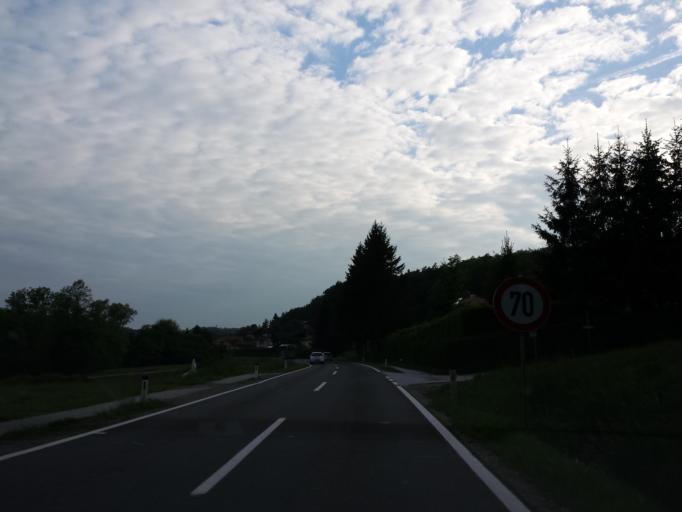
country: AT
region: Styria
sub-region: Politischer Bezirk Graz-Umgebung
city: Eggersdorf bei Graz
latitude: 47.1096
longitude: 15.6178
